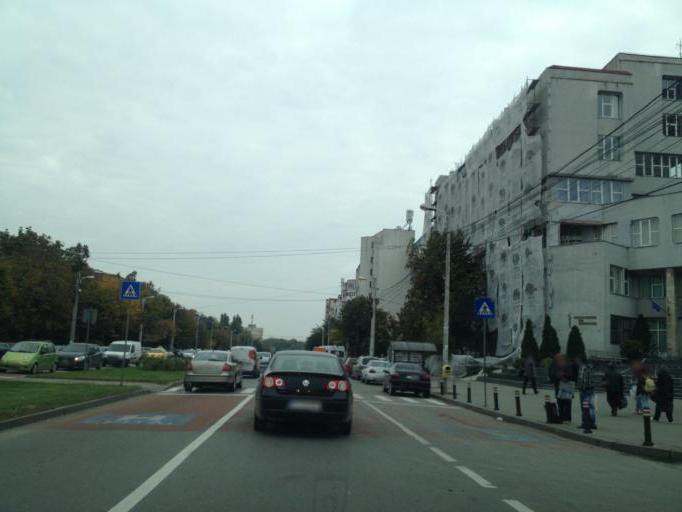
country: RO
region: Dolj
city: Craiova
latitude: 44.3060
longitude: 23.7943
